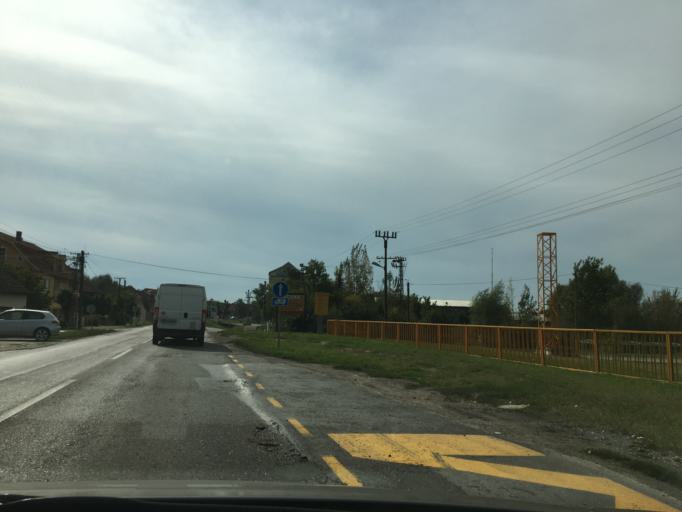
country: RS
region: Autonomna Pokrajina Vojvodina
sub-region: Juznobacki Okrug
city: Temerin
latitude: 45.3770
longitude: 19.8757
